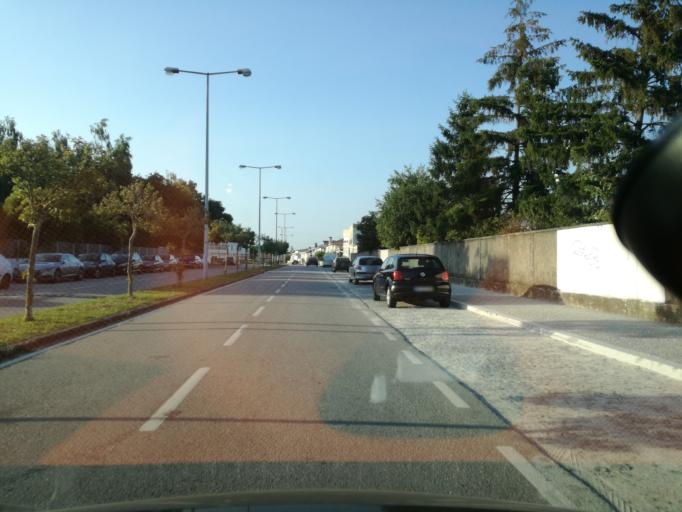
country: PT
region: Porto
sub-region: Maia
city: Milheiros
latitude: 41.2144
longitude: -8.6001
